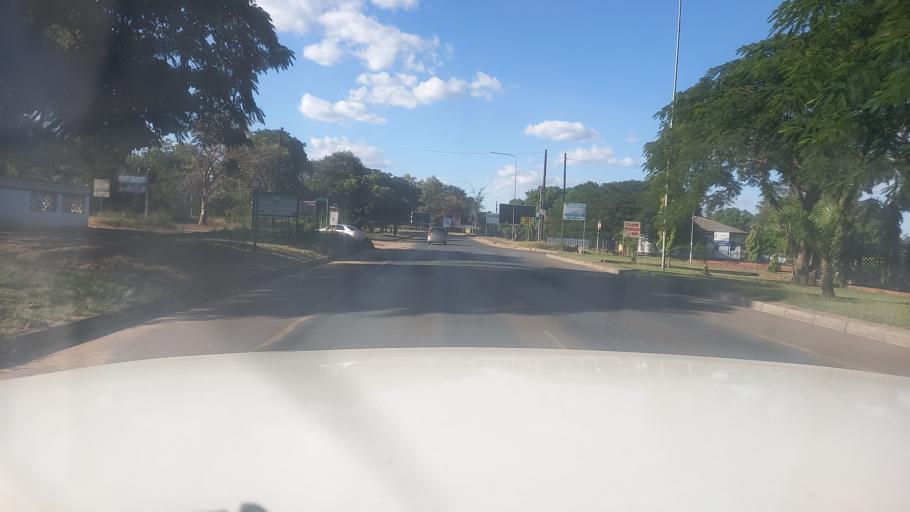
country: ZM
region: Southern
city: Livingstone
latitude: -17.8403
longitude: 25.8633
